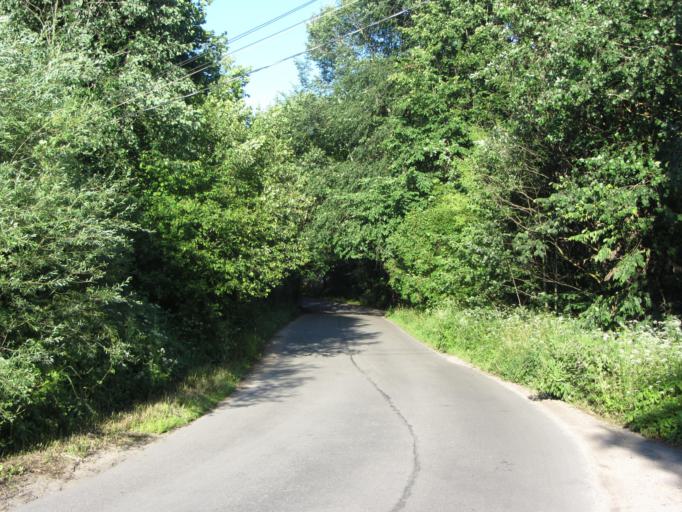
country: LT
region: Vilnius County
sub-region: Vilnius
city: Vilnius
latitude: 54.7480
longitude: 25.3048
